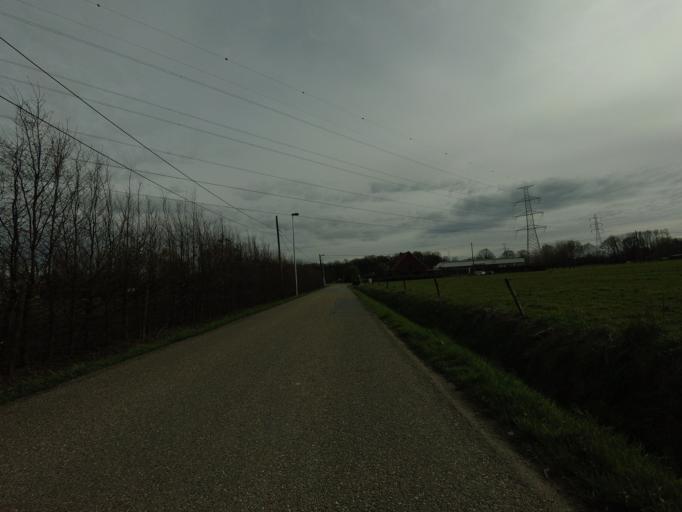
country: BE
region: Flanders
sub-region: Provincie Antwerpen
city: Lint
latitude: 51.1368
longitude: 4.5160
